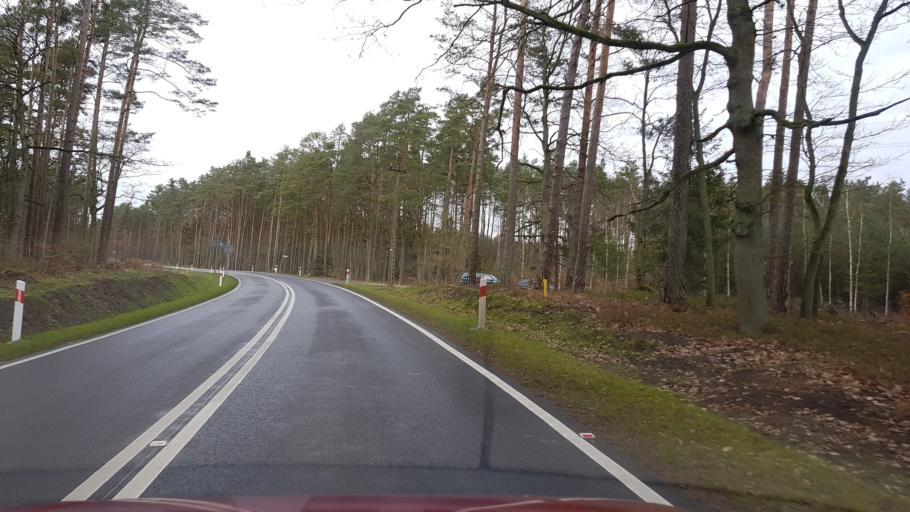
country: PL
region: West Pomeranian Voivodeship
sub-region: Powiat policki
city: Police
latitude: 53.6547
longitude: 14.4792
